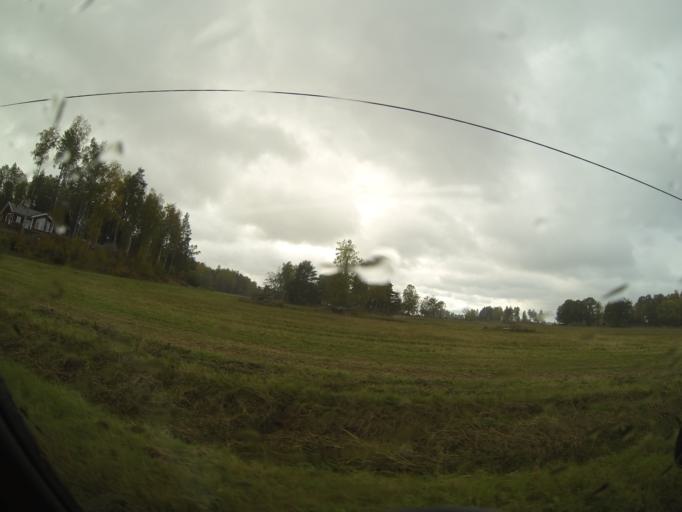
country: SE
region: Soedermanland
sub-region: Eskilstuna Kommun
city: Kvicksund
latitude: 59.3371
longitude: 16.3001
